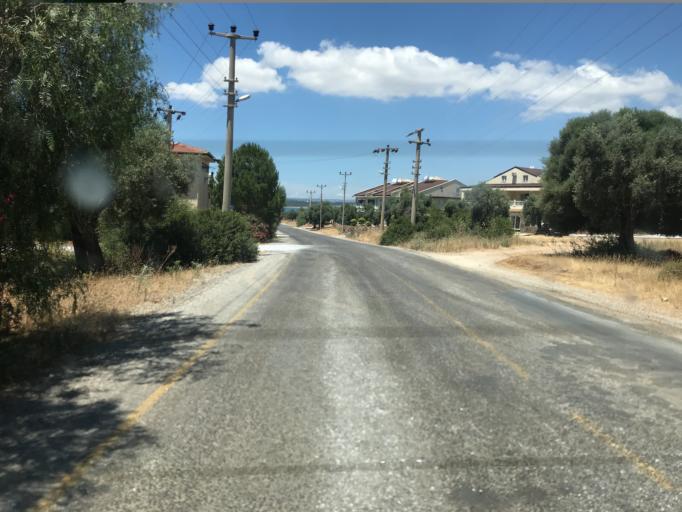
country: TR
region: Aydin
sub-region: Didim
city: Didim
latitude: 37.4003
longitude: 27.4353
